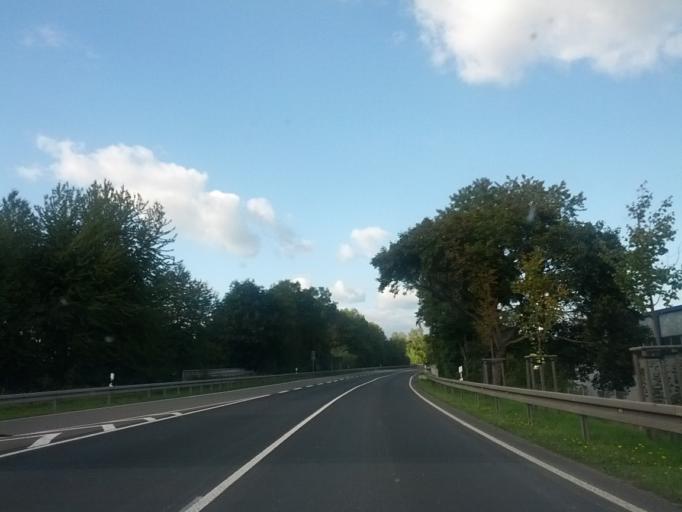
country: DE
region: Thuringia
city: Fambach
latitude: 50.7430
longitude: 10.3565
